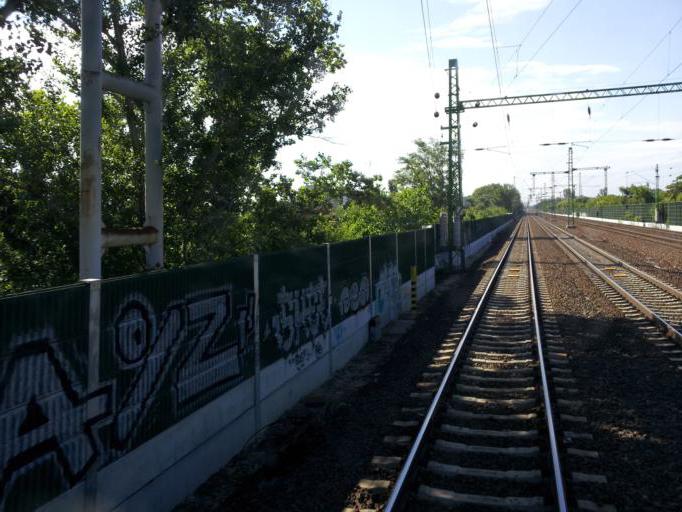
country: HU
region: Budapest
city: Budapest XI. keruelet
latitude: 47.4513
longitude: 19.0271
